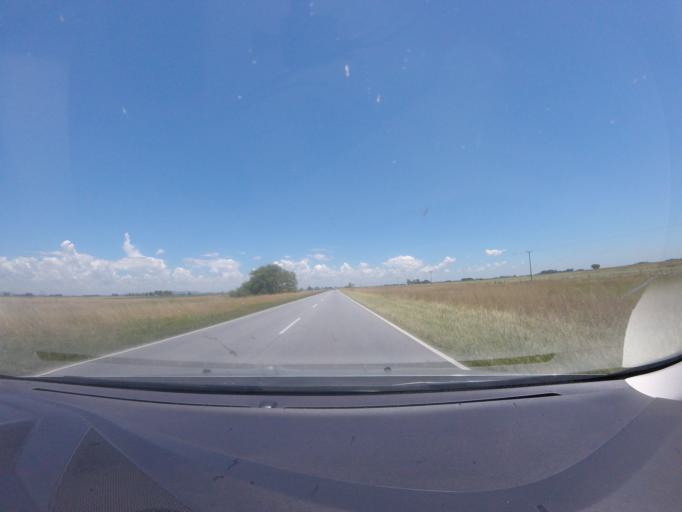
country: AR
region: Buenos Aires
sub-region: Partido de Tandil
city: Tandil
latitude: -37.1697
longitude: -59.0295
